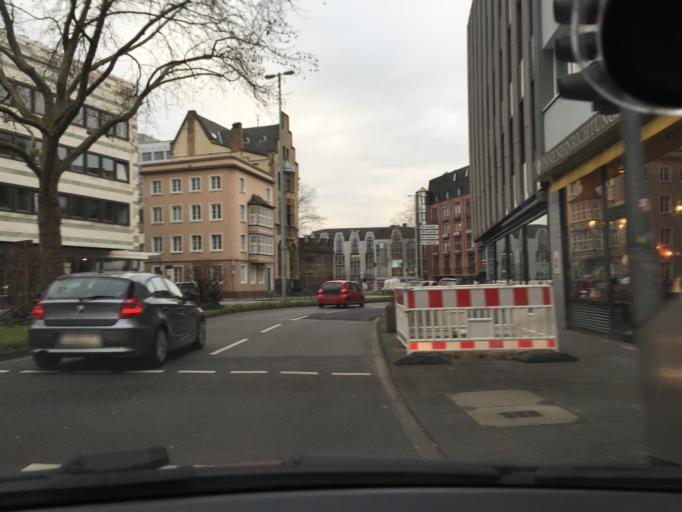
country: DE
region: North Rhine-Westphalia
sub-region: Regierungsbezirk Koln
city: Neustadt/Nord
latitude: 50.9412
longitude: 6.9478
